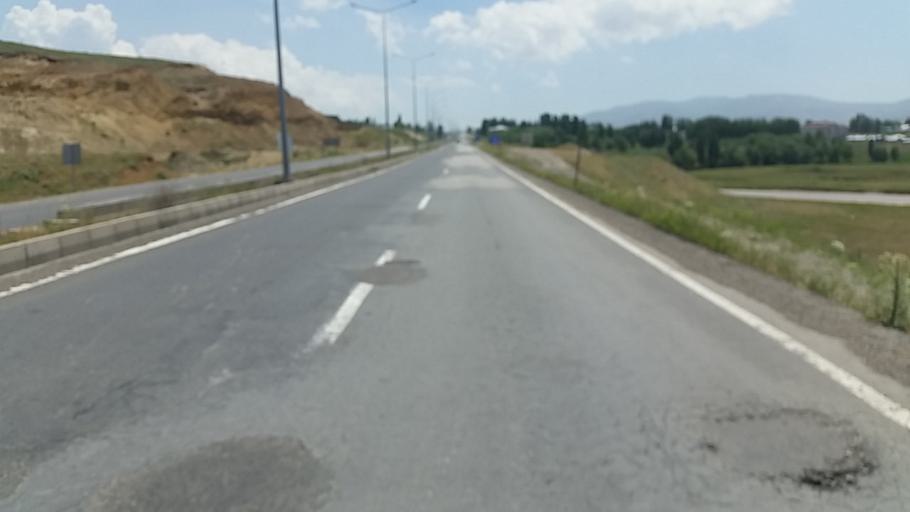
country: TR
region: Agri
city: Taslicay
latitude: 39.6483
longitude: 43.3646
